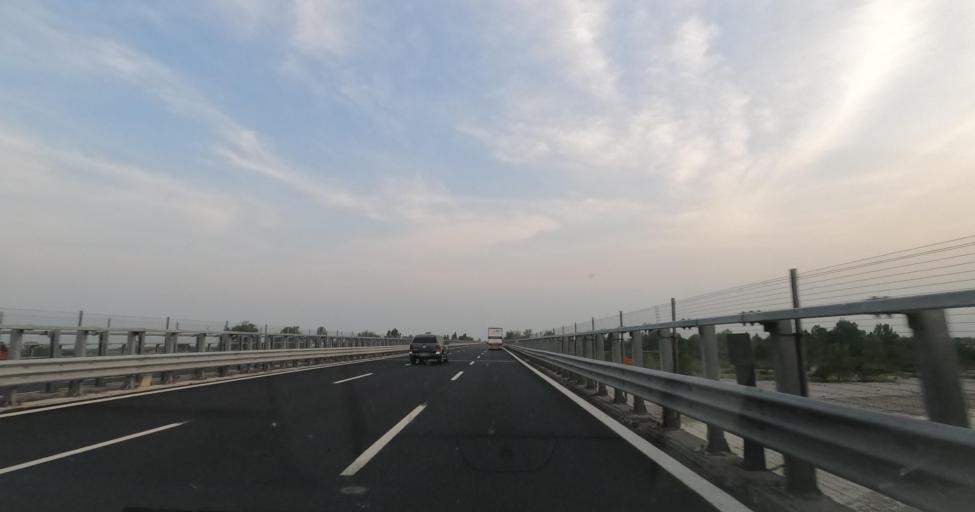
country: IT
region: Veneto
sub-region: Provincia di Treviso
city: Spresiano
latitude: 45.7901
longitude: 12.2929
